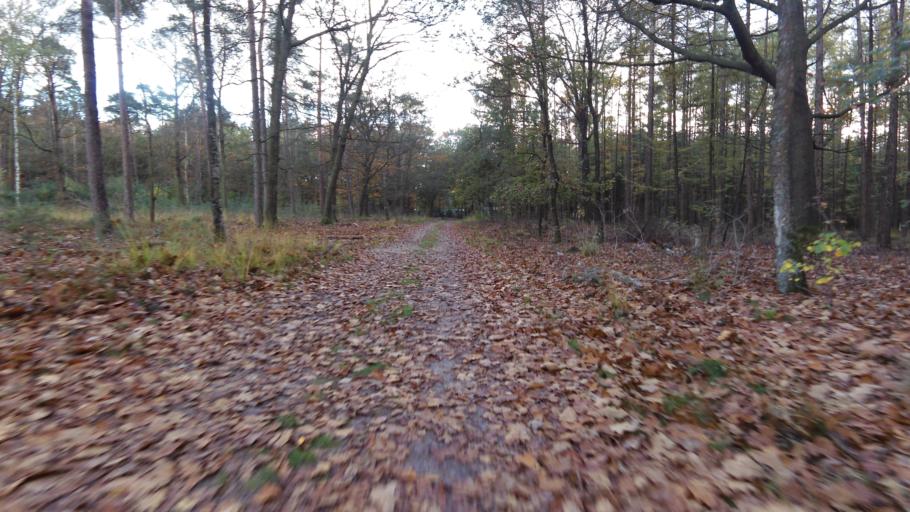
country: NL
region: Gelderland
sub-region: Gemeente Nunspeet
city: Nunspeet
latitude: 52.3529
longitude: 5.8260
